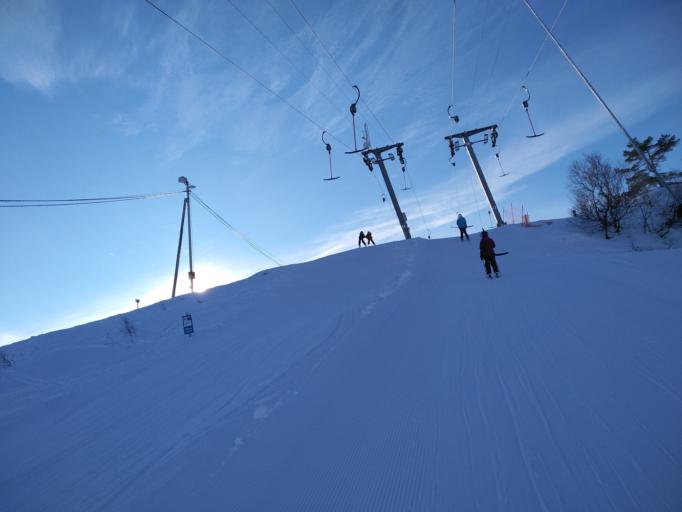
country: NO
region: Rogaland
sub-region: Sauda
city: Sauda
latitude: 59.6195
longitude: 6.2353
